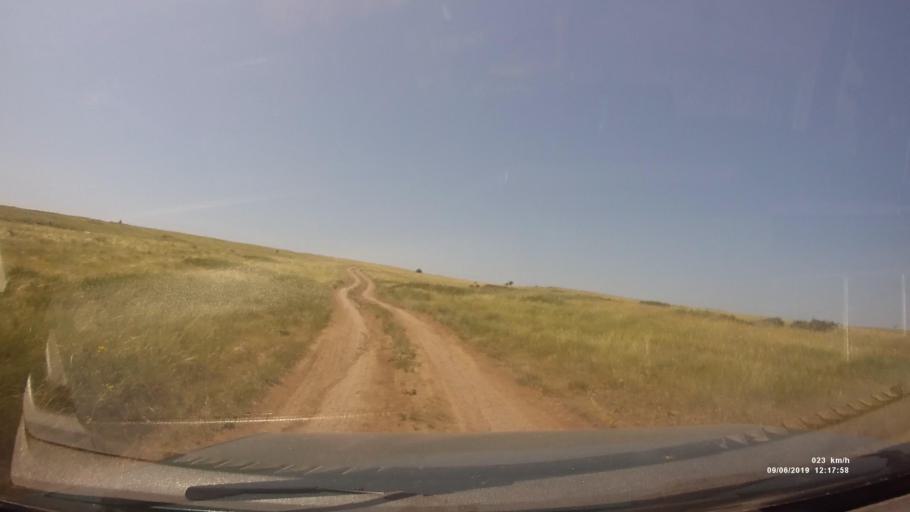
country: RU
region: Rostov
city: Kamensk-Shakhtinskiy
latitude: 48.2557
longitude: 40.3124
